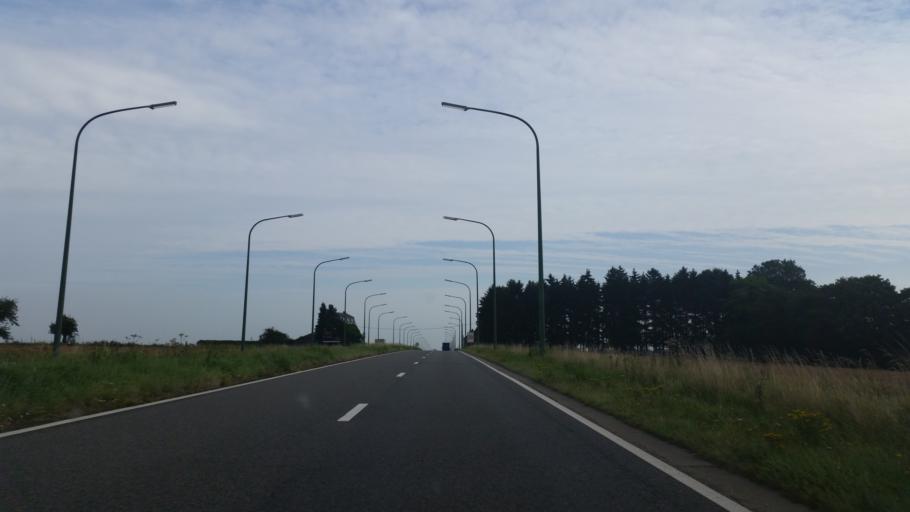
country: BE
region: Wallonia
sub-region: Province de Liege
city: Tinlot
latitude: 50.4938
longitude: 5.3883
